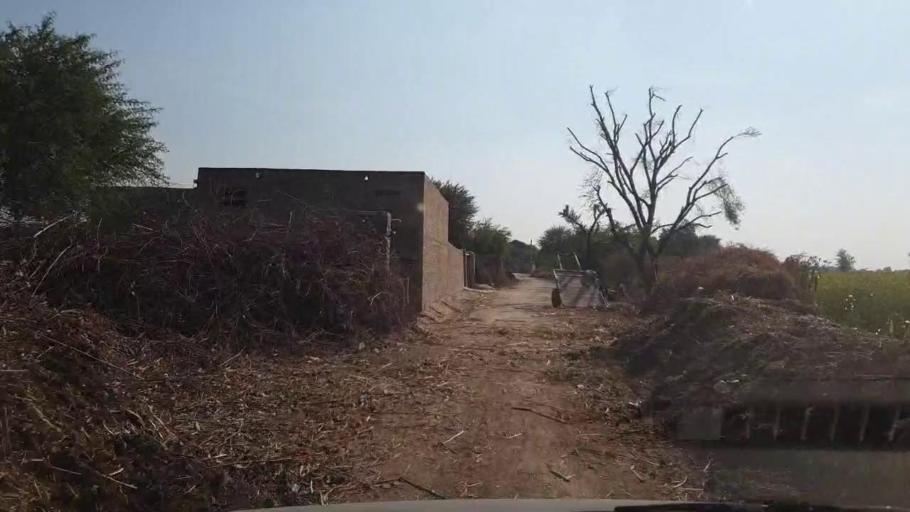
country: PK
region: Sindh
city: Chambar
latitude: 25.3253
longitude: 68.7978
